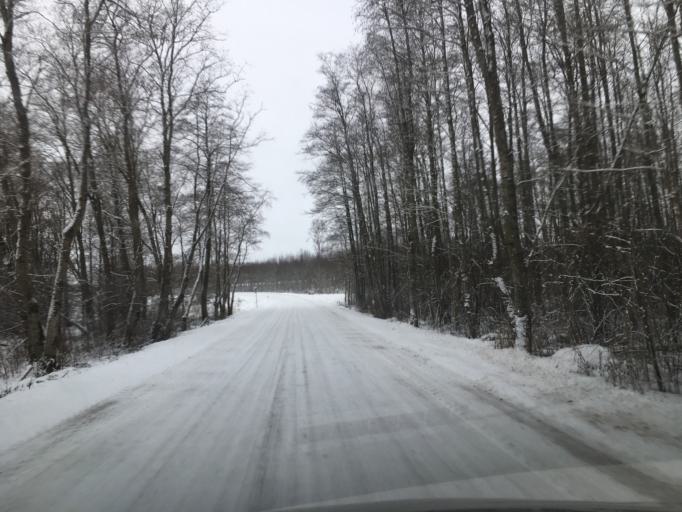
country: EE
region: Tartu
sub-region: Elva linn
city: Elva
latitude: 58.1899
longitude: 26.2744
